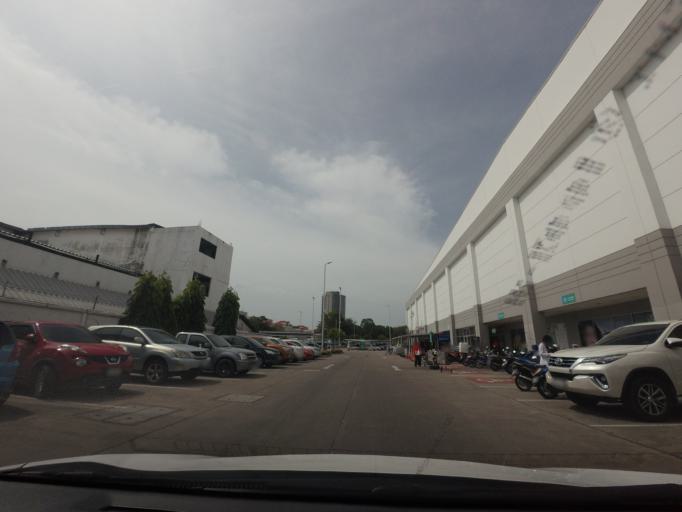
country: TH
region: Chon Buri
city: Phatthaya
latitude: 12.9512
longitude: 100.8930
